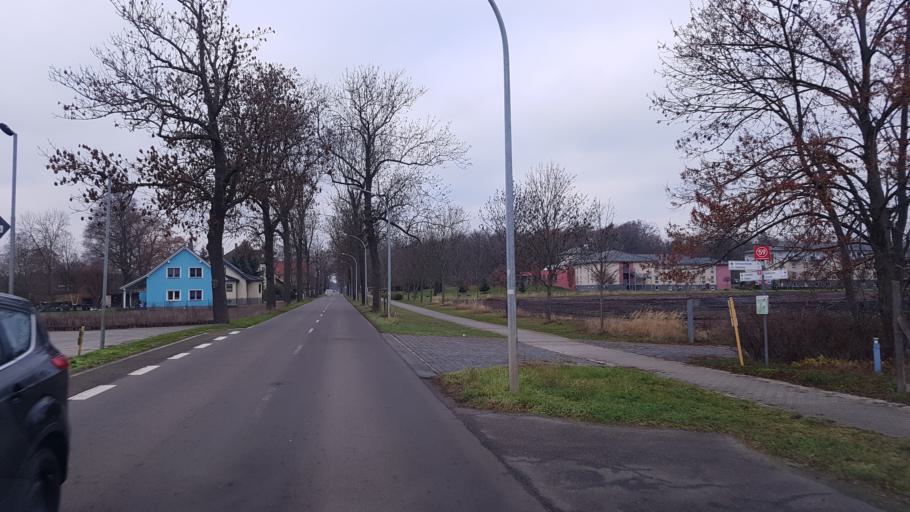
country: DE
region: Brandenburg
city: Schipkau
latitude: 51.5601
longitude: 13.8885
